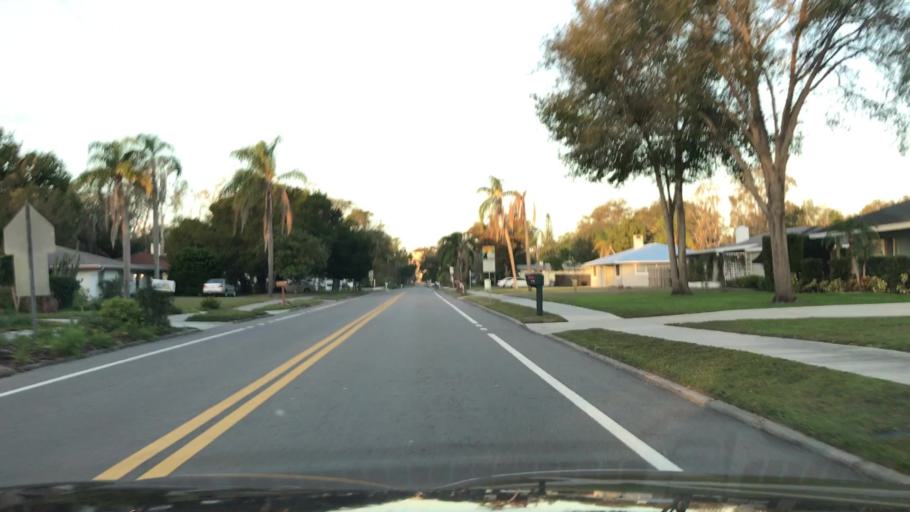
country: US
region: Florida
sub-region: Sarasota County
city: Sarasota
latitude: 27.3365
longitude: -82.5149
